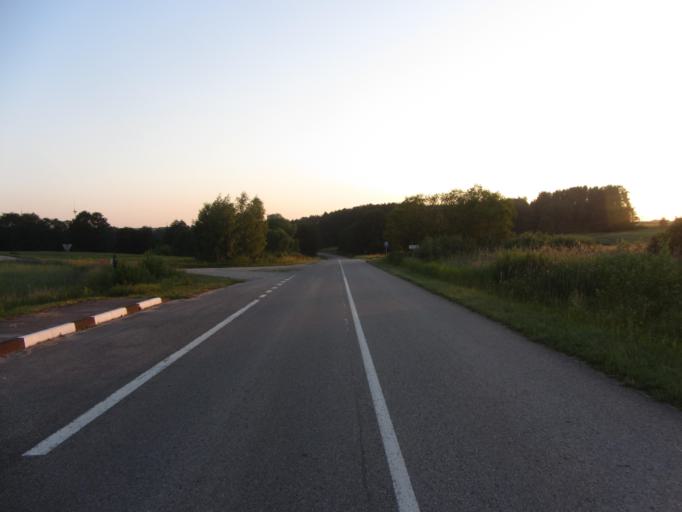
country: LT
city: Veisiejai
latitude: 54.2304
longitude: 23.8539
